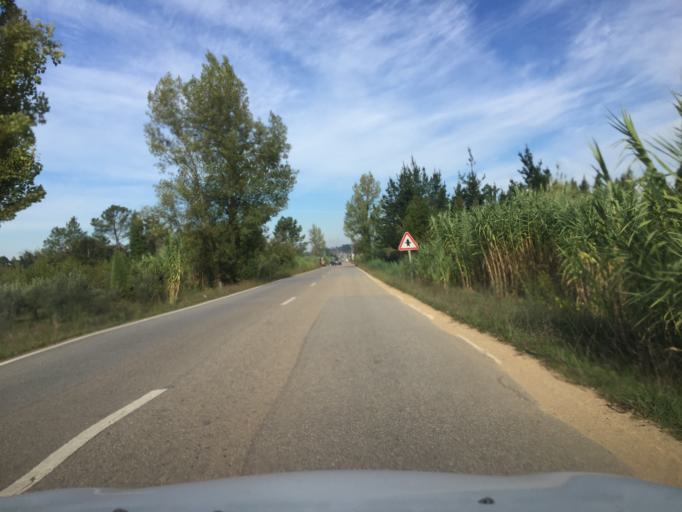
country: PT
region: Aveiro
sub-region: Anadia
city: Anadia
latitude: 40.4360
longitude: -8.4188
